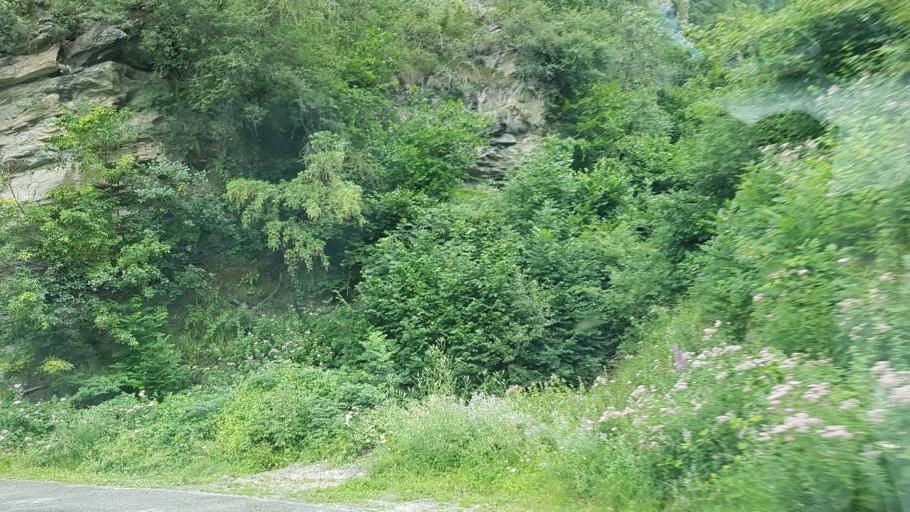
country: IT
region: Piedmont
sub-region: Provincia di Cuneo
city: Stroppo
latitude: 44.5204
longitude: 7.1164
